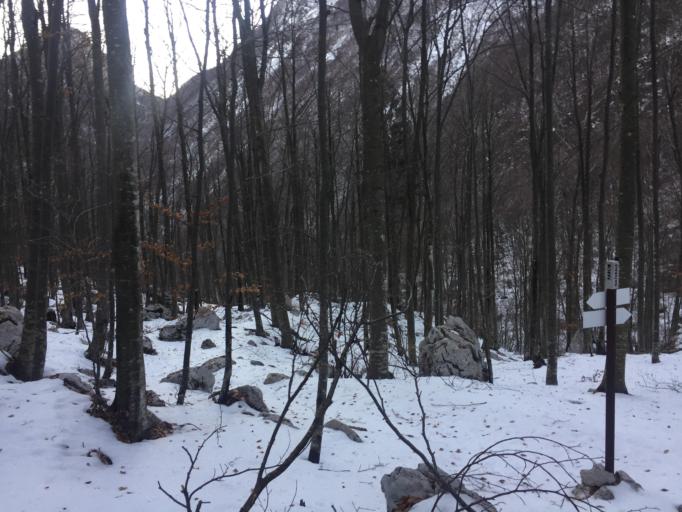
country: IT
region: Friuli Venezia Giulia
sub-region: Provincia di Udine
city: Prato
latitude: 46.3462
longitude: 13.2828
